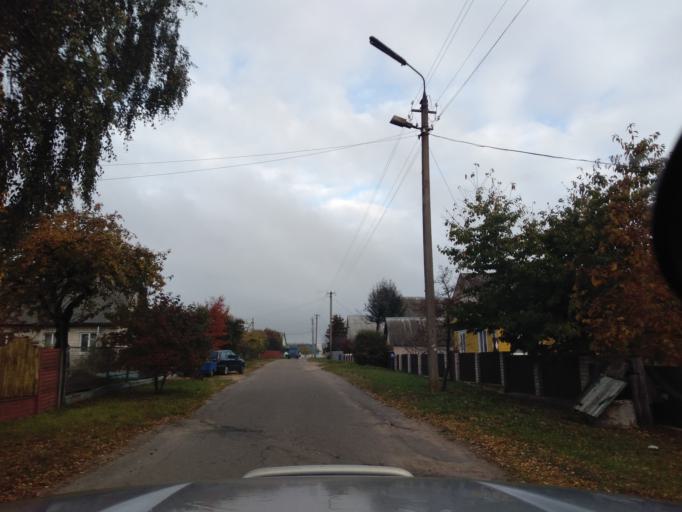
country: BY
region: Minsk
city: Kapyl'
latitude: 53.1595
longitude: 27.0825
